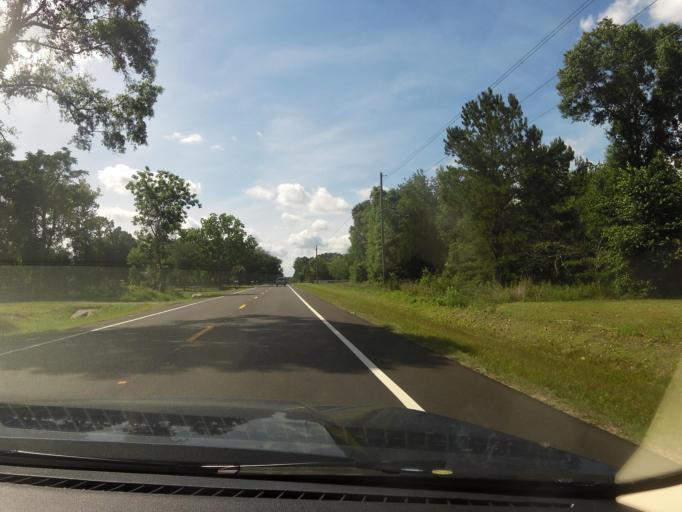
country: US
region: Florida
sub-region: Nassau County
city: Hilliard
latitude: 30.6201
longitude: -81.8852
